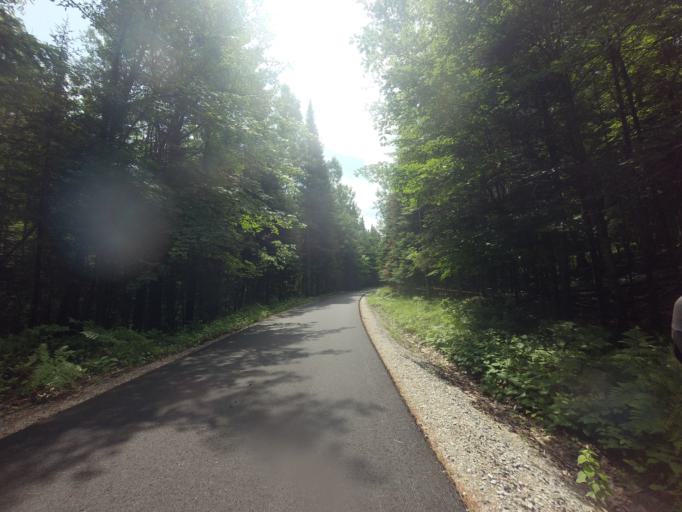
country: CA
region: Quebec
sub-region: Outaouais
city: Maniwaki
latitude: 46.1309
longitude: -76.0329
